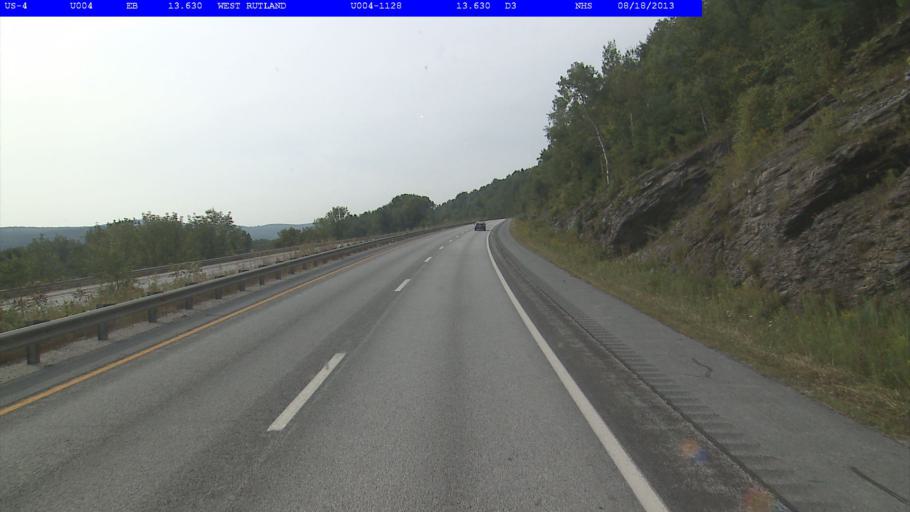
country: US
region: Vermont
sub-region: Rutland County
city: West Rutland
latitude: 43.5983
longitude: -73.0578
